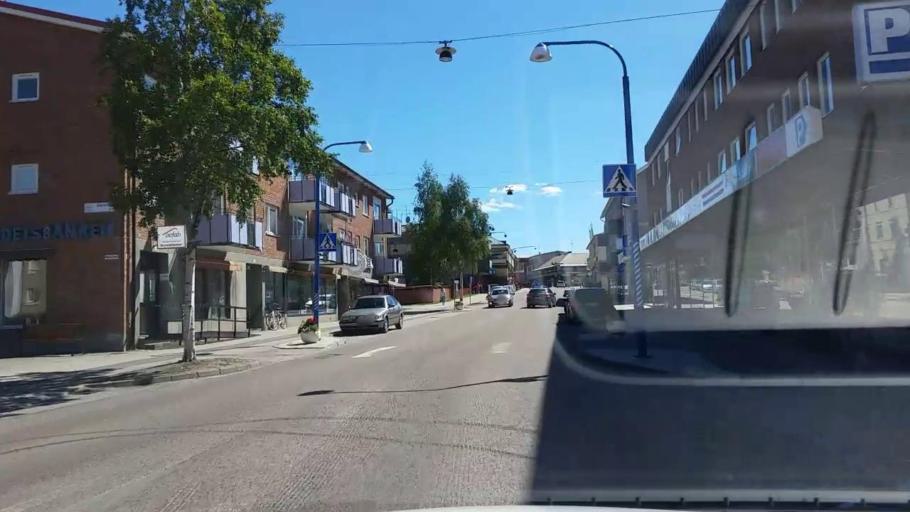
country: SE
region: Gaevleborg
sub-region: Ovanakers Kommun
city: Edsbyn
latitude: 61.3755
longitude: 15.8183
